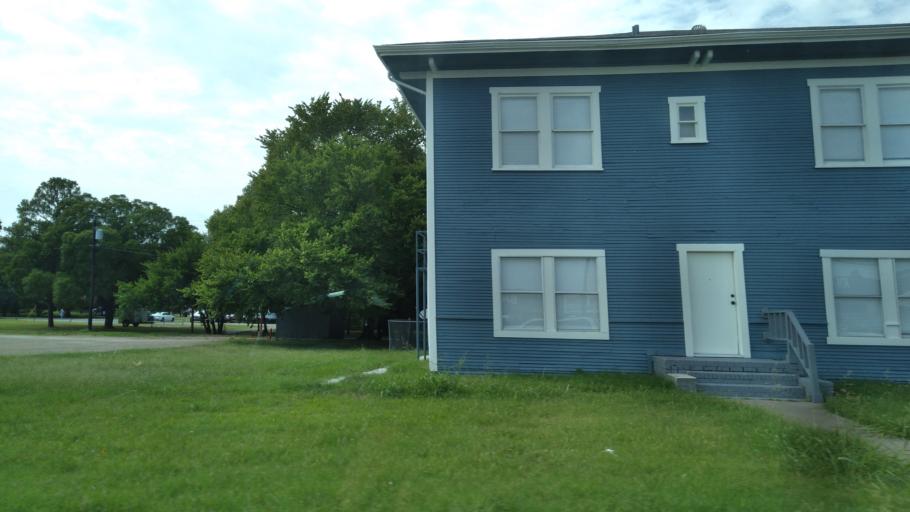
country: US
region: Texas
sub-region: Navarro County
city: Corsicana
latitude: 32.0823
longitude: -96.4832
